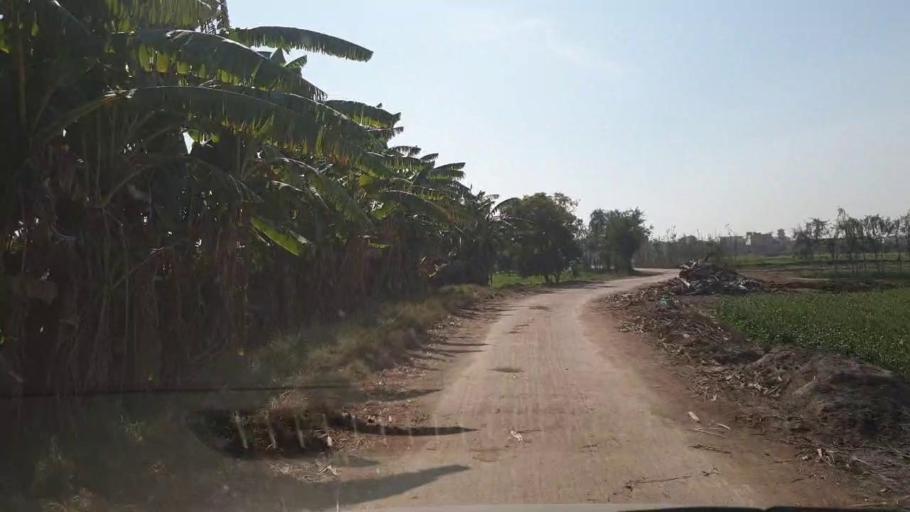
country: PK
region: Sindh
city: Tando Allahyar
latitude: 25.3924
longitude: 68.7819
